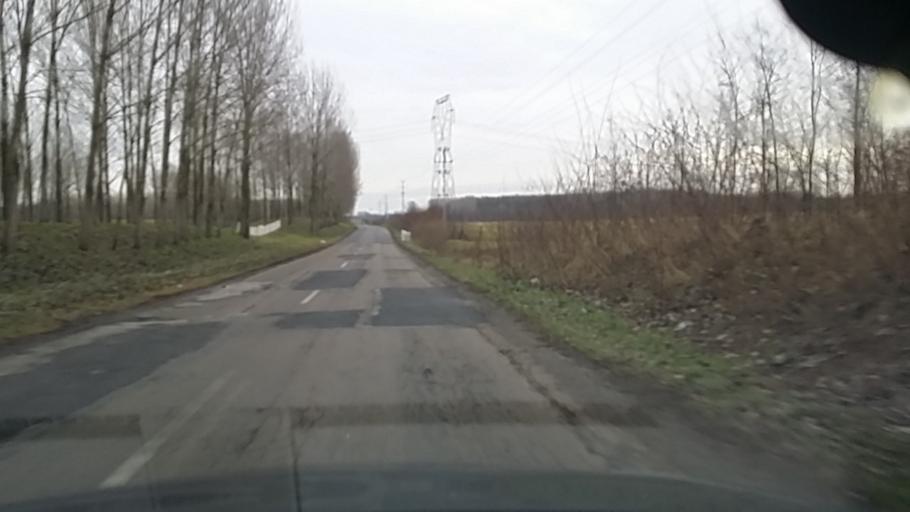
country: HU
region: Szabolcs-Szatmar-Bereg
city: Kek
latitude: 48.0896
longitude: 21.8695
